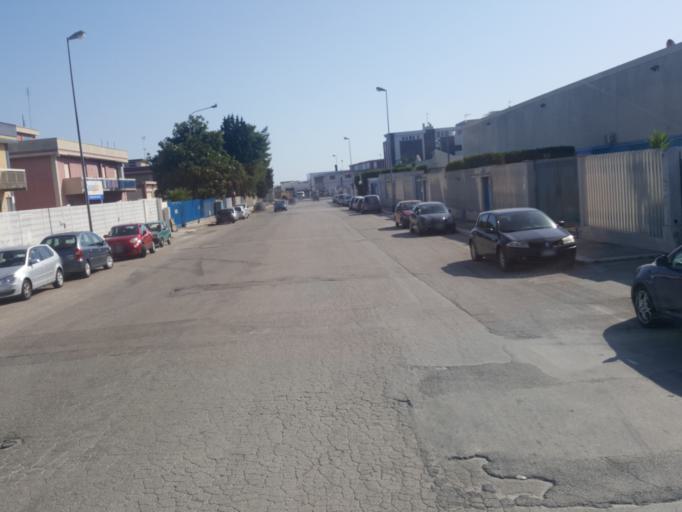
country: IT
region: Apulia
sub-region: Provincia di Barletta - Andria - Trani
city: Barletta
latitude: 41.3076
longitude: 16.3103
